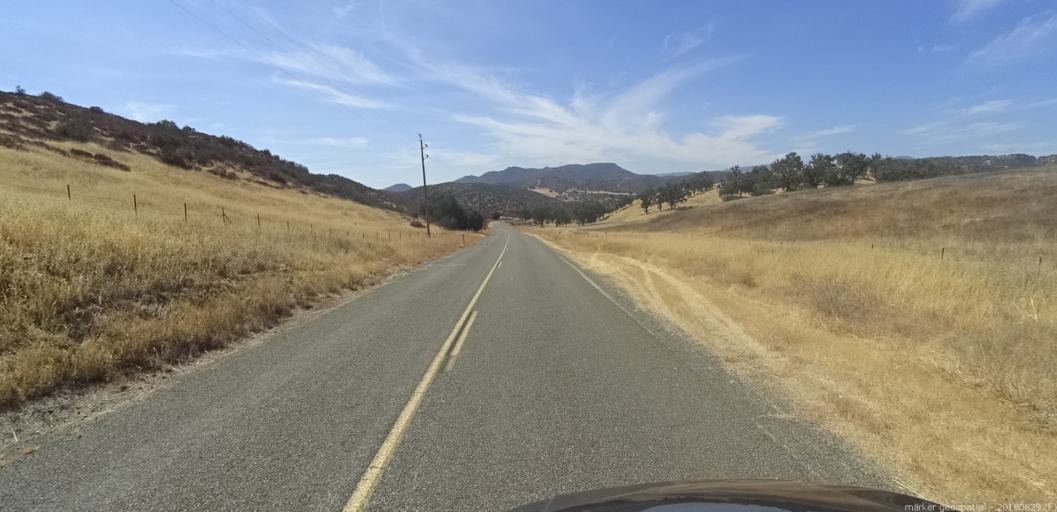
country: US
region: California
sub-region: San Luis Obispo County
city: Lake Nacimiento
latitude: 35.8240
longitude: -120.9805
